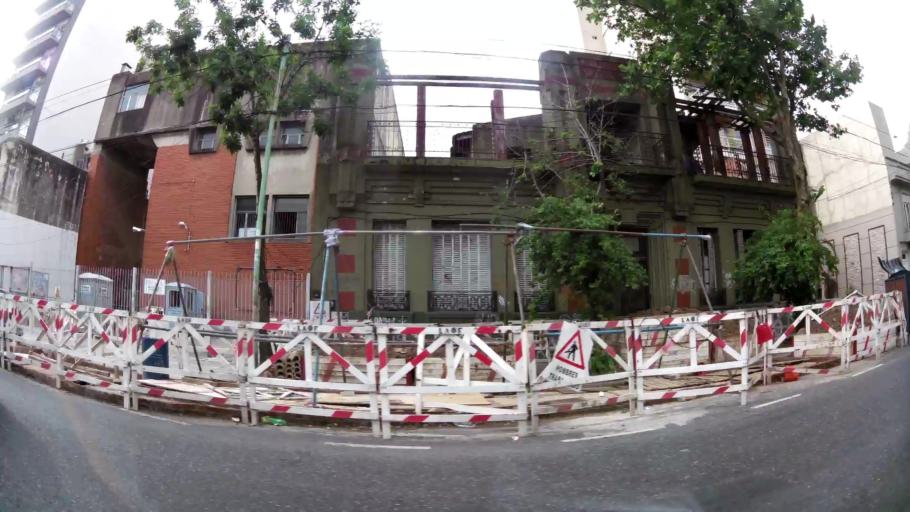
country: AR
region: Buenos Aires F.D.
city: Villa Santa Rita
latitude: -34.6322
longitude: -58.4652
